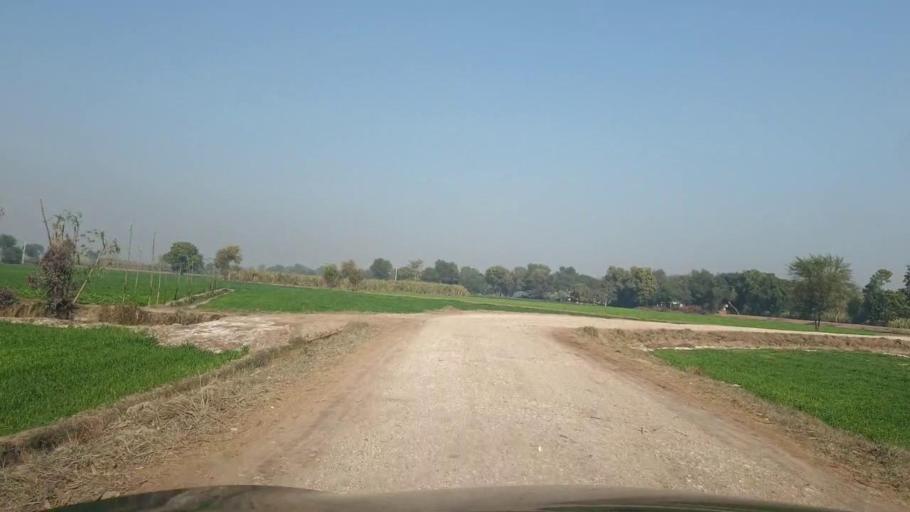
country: PK
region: Sindh
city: Ubauro
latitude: 28.1135
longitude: 69.7479
